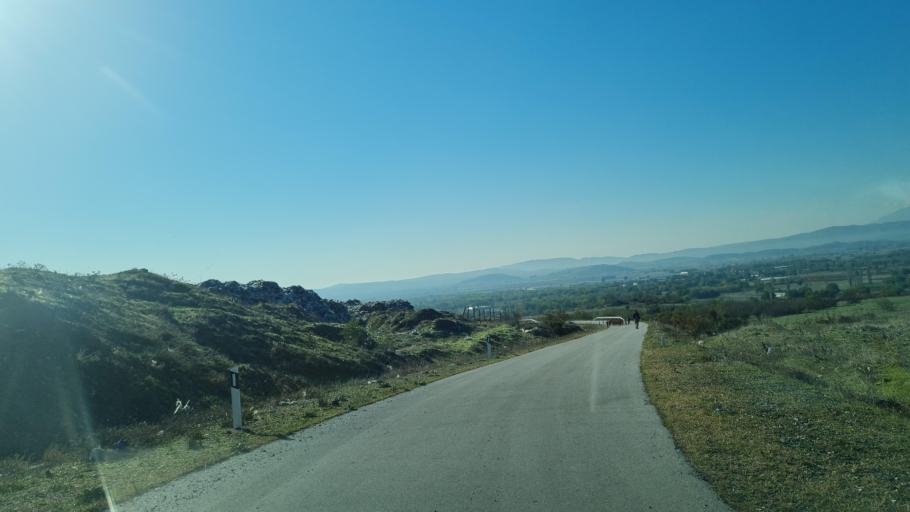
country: MK
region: Bogdanci
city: Bogdanci
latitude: 41.1997
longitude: 22.5618
